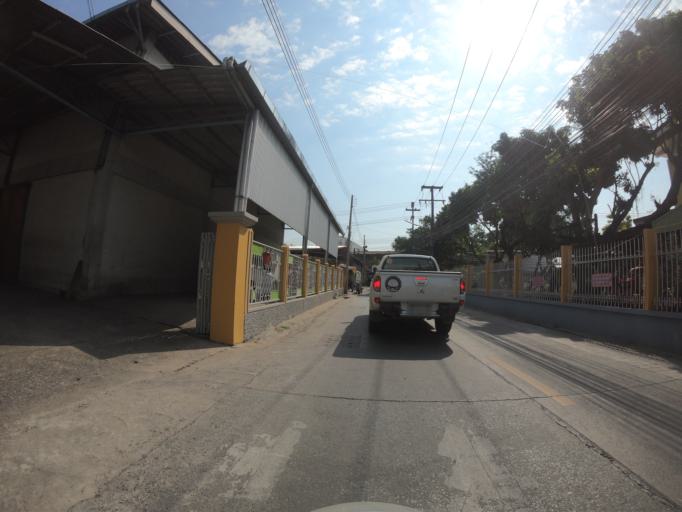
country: TH
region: Chiang Mai
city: Chiang Mai
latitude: 18.7985
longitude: 99.0000
